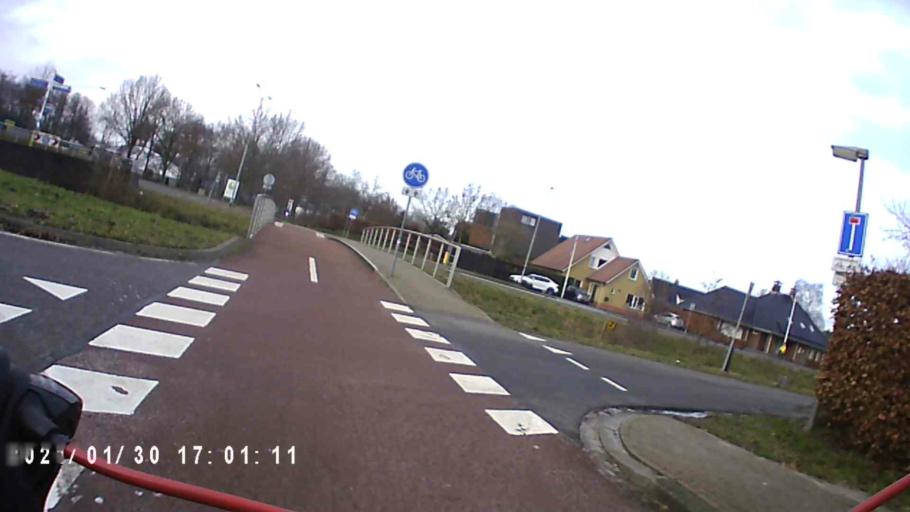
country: NL
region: Groningen
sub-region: Gemeente Leek
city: Leek
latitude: 53.1507
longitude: 6.3722
